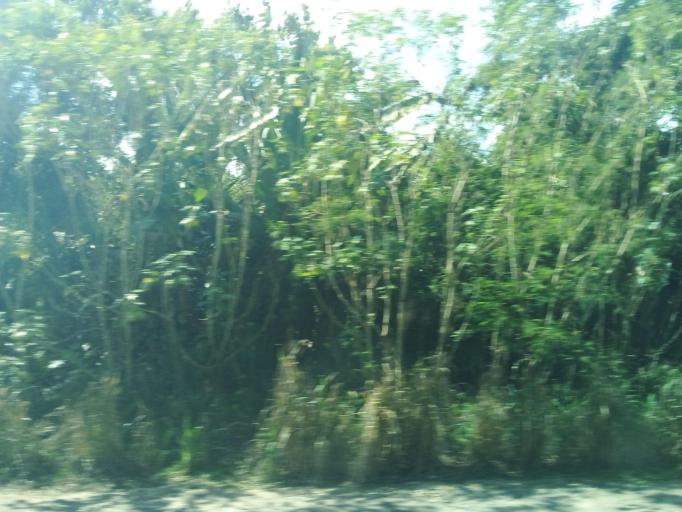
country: BR
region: Minas Gerais
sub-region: Governador Valadares
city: Governador Valadares
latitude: -18.8728
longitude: -41.7805
